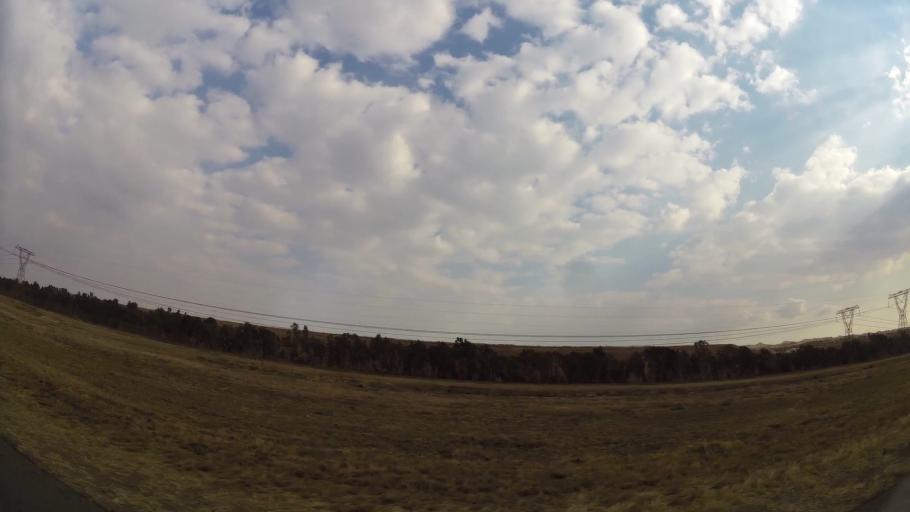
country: ZA
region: Gauteng
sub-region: Ekurhuleni Metropolitan Municipality
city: Springs
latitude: -26.2907
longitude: 28.5415
